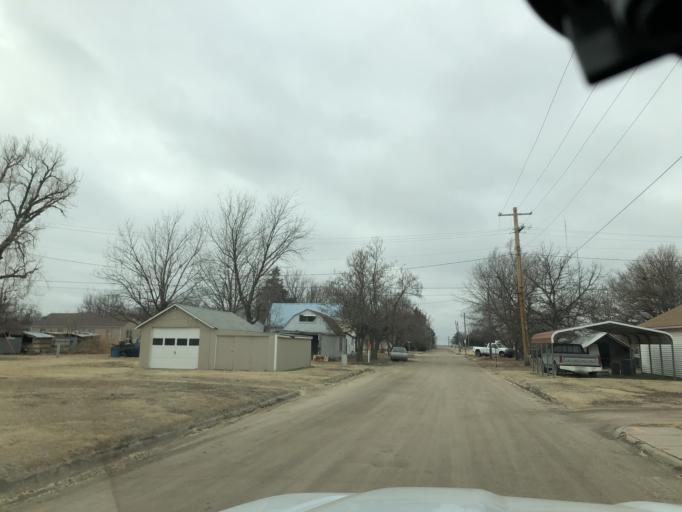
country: US
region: Kansas
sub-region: Stafford County
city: Stafford
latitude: 37.9674
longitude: -98.6005
